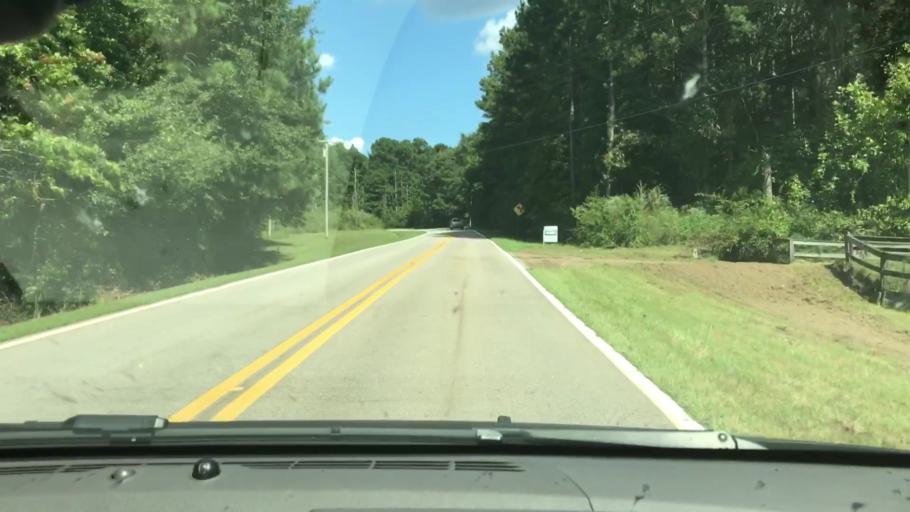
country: US
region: Georgia
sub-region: Troup County
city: La Grange
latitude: 33.1415
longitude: -85.0943
